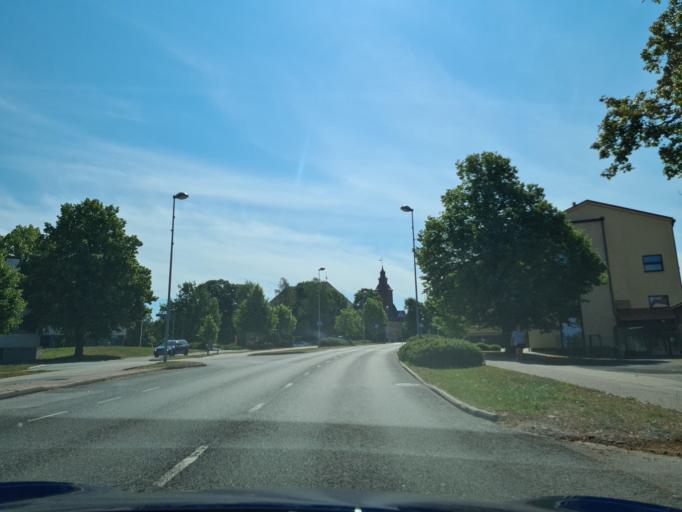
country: FI
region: Varsinais-Suomi
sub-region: Turku
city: Paimio
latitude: 60.4558
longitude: 22.6903
